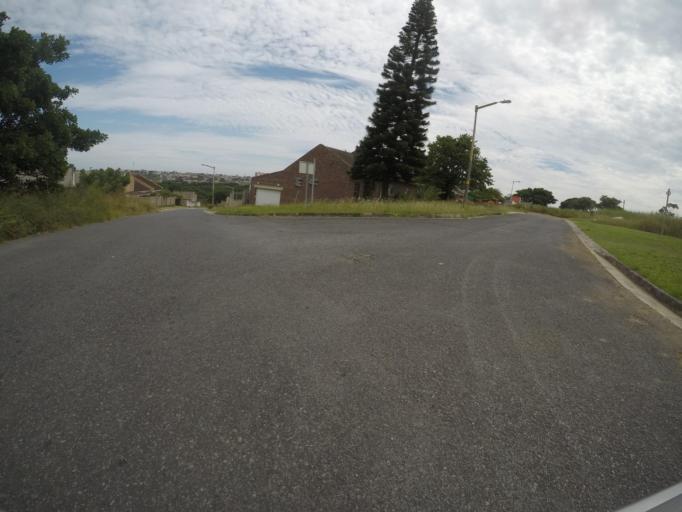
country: ZA
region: Eastern Cape
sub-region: Buffalo City Metropolitan Municipality
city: East London
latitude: -33.0017
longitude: 27.8821
